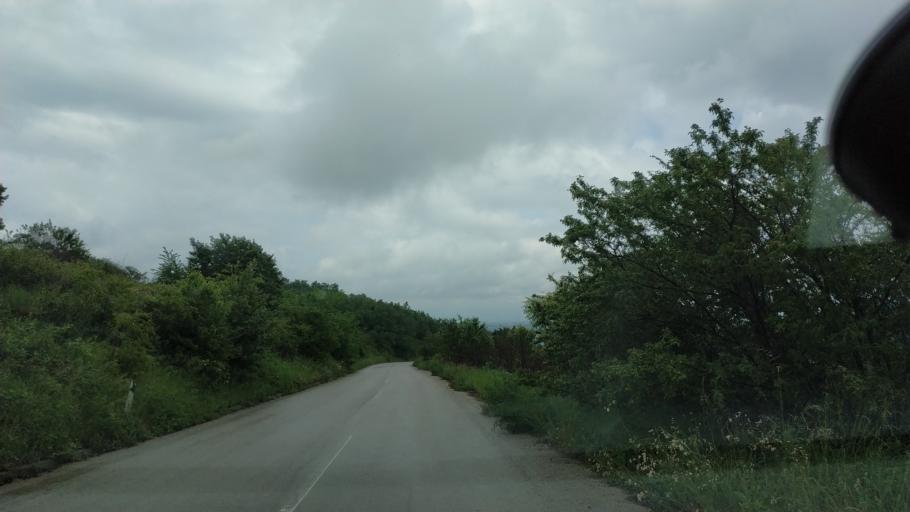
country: RS
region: Central Serbia
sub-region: Toplicki Okrug
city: Prokuplje
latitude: 43.4120
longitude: 21.5526
